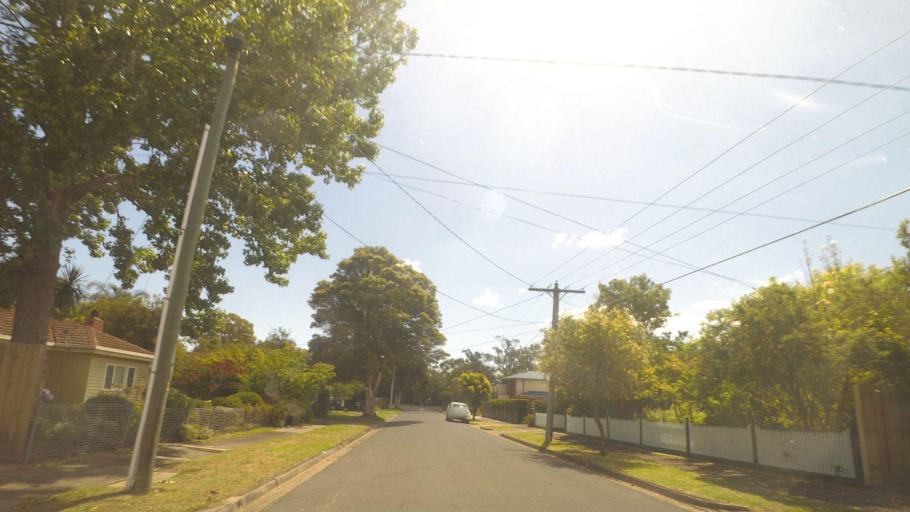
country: AU
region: Victoria
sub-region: Yarra Ranges
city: Kilsyth
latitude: -37.8075
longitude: 145.3167
